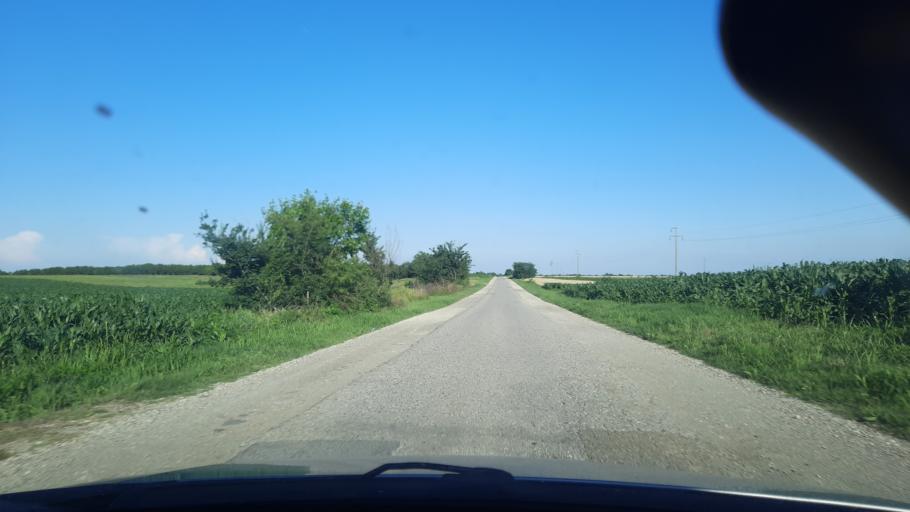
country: RS
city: Cortanovci
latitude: 45.1123
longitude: 19.9682
